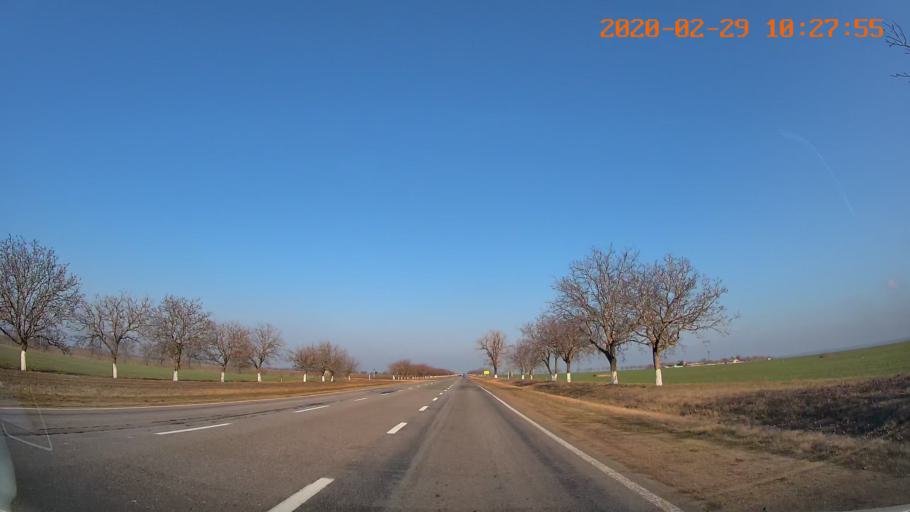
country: MD
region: Telenesti
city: Tiraspolul Nou
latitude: 46.9030
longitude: 29.5947
